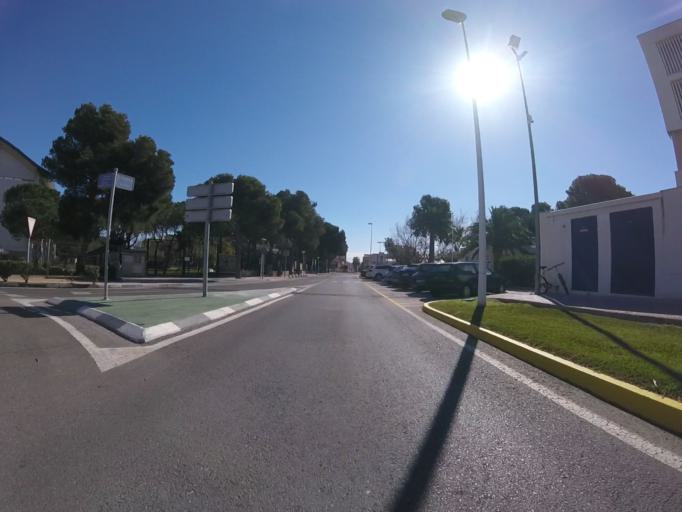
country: ES
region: Valencia
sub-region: Provincia de Castello
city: Orpesa/Oropesa del Mar
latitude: 40.0931
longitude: 0.1307
